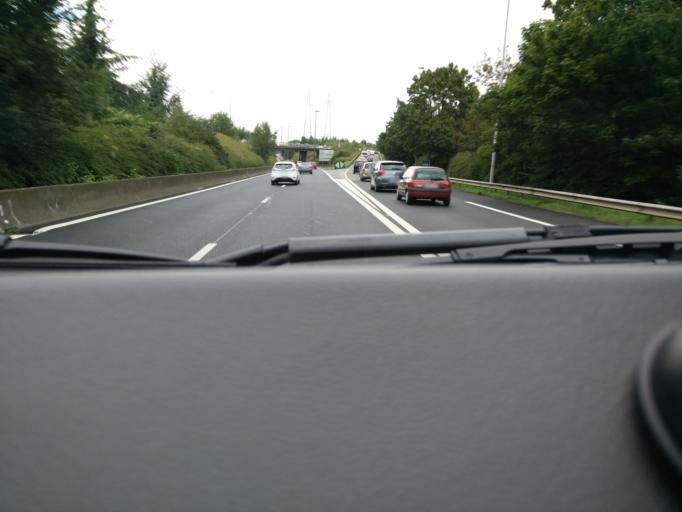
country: FR
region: Nord-Pas-de-Calais
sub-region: Departement du Nord
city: Wasquehal
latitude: 50.6671
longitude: 3.1153
